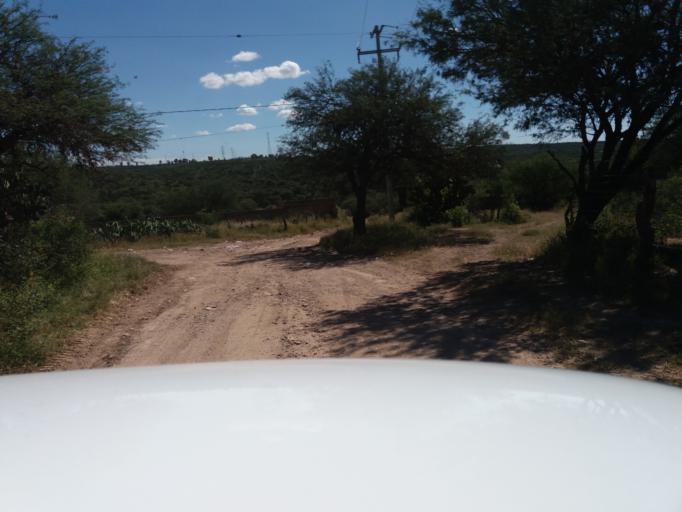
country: MX
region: Aguascalientes
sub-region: Aguascalientes
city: San Sebastian [Fraccionamiento]
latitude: 21.7749
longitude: -102.2296
